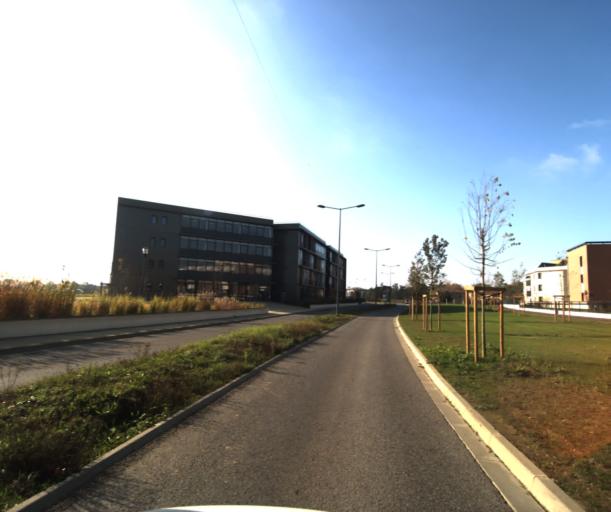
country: FR
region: Midi-Pyrenees
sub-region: Departement de la Haute-Garonne
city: Colomiers
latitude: 43.5978
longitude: 1.3515
